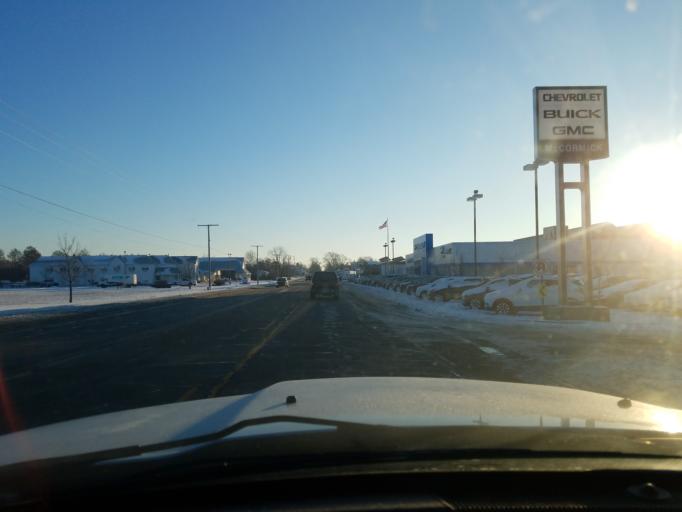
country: US
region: Indiana
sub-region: Elkhart County
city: Nappanee
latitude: 41.4427
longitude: -86.0177
